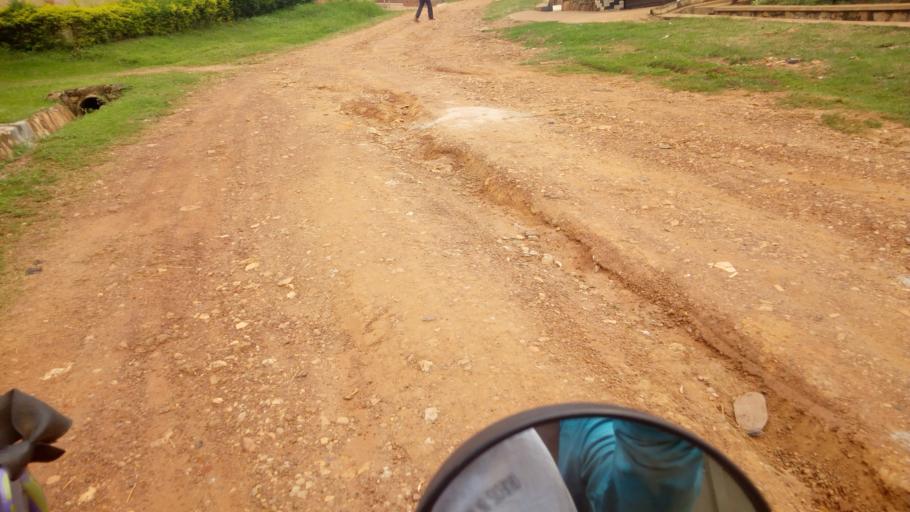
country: UG
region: Central Region
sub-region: Wakiso District
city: Kireka
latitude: 0.3190
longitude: 32.6534
